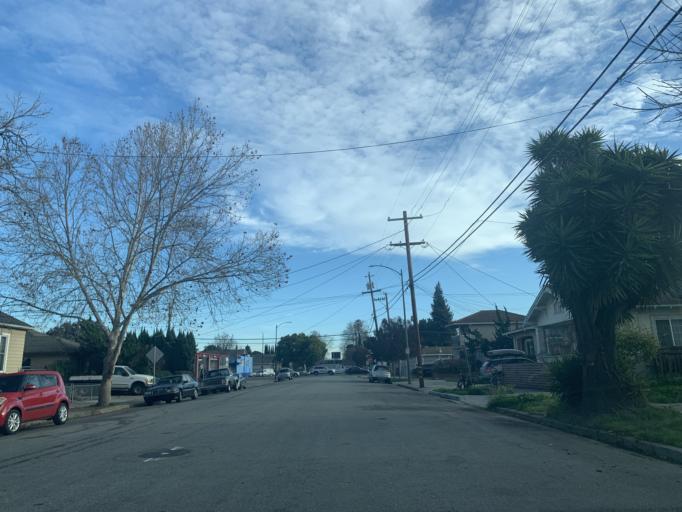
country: US
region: California
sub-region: Santa Clara County
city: San Jose
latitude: 37.3241
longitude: -121.8716
